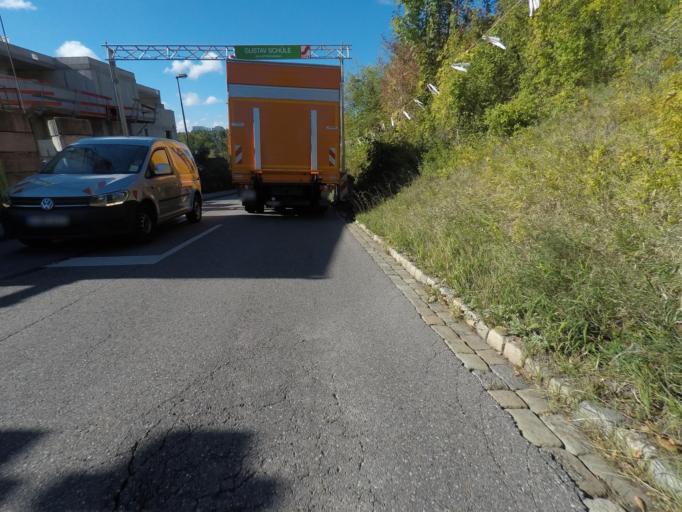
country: DE
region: Baden-Wuerttemberg
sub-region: Regierungsbezirk Stuttgart
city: Stuttgart
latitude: 48.7474
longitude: 9.1216
